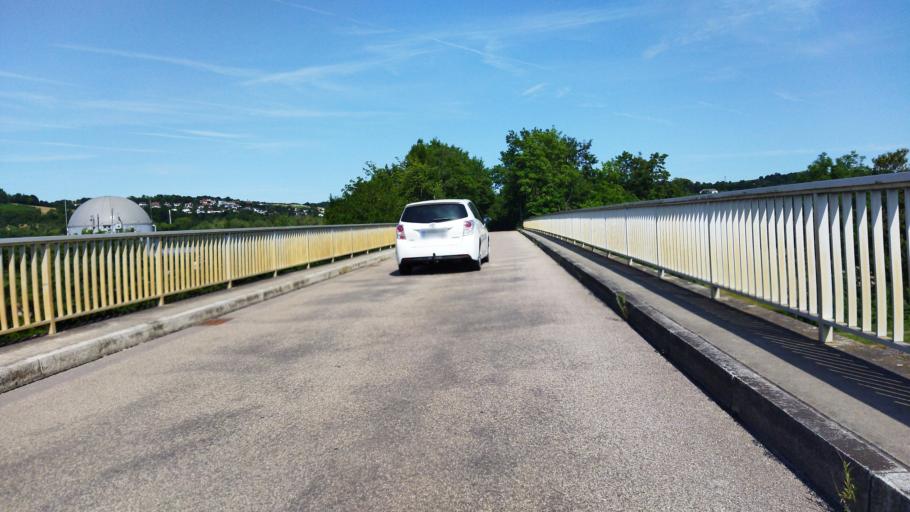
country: DE
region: Bavaria
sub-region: Lower Bavaria
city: Bad Abbach
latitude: 48.9363
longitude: 12.0259
